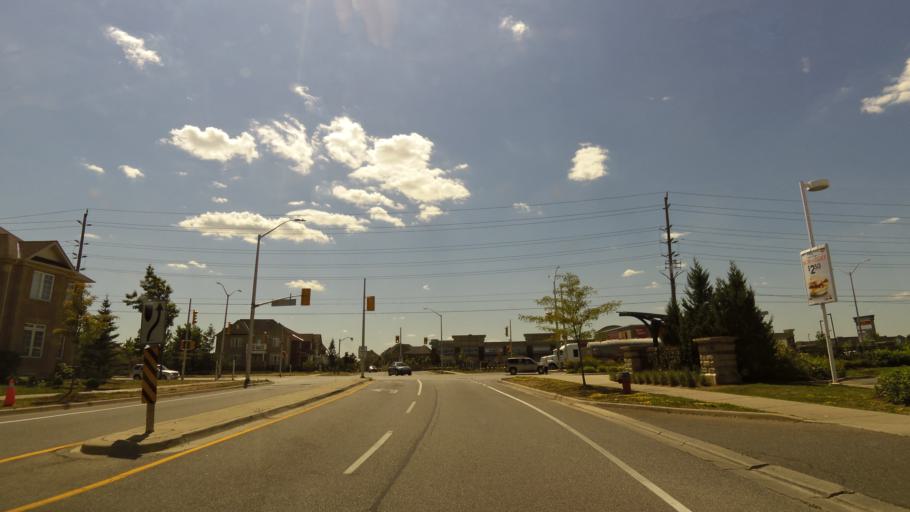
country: CA
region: Ontario
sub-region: Halton
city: Milton
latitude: 43.6302
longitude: -79.8754
